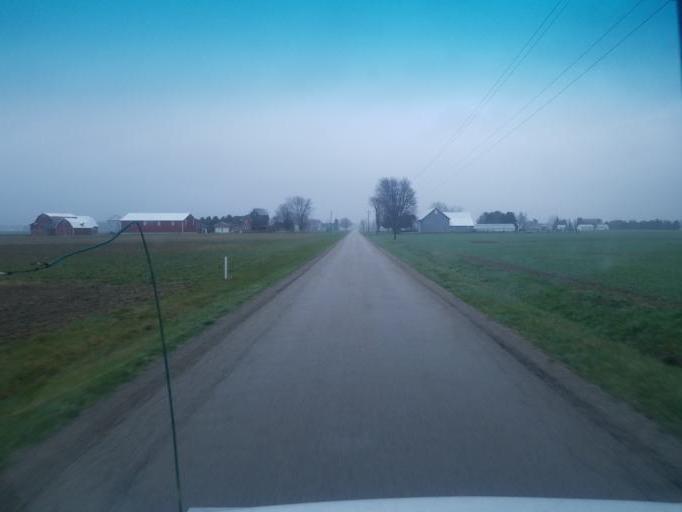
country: US
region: Ohio
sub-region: Fulton County
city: Archbold
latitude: 41.4239
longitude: -84.2478
